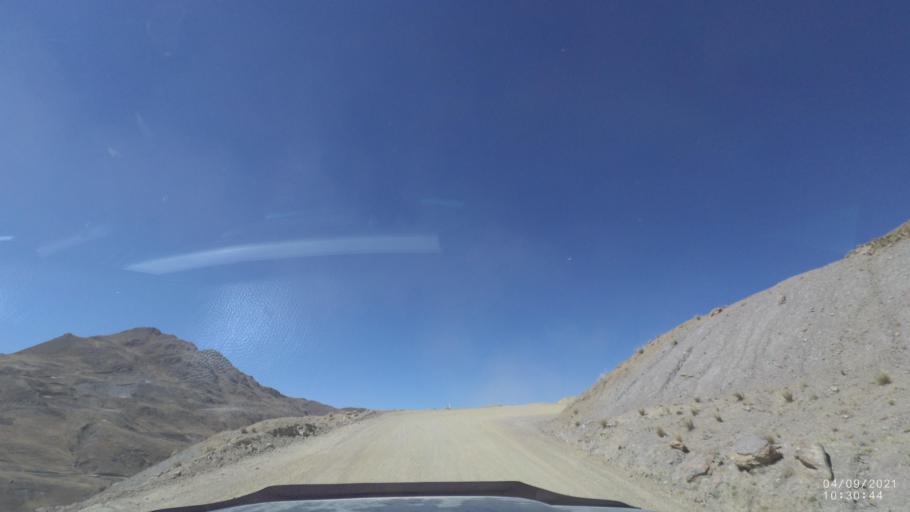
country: BO
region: Cochabamba
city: Sipe Sipe
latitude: -17.3033
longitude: -66.4442
